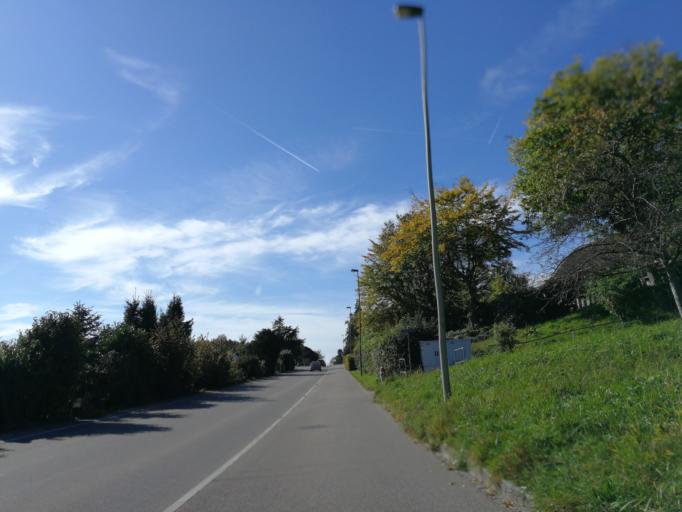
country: CH
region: Zurich
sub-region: Bezirk Meilen
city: Uerikon
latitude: 47.2494
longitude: 8.7572
